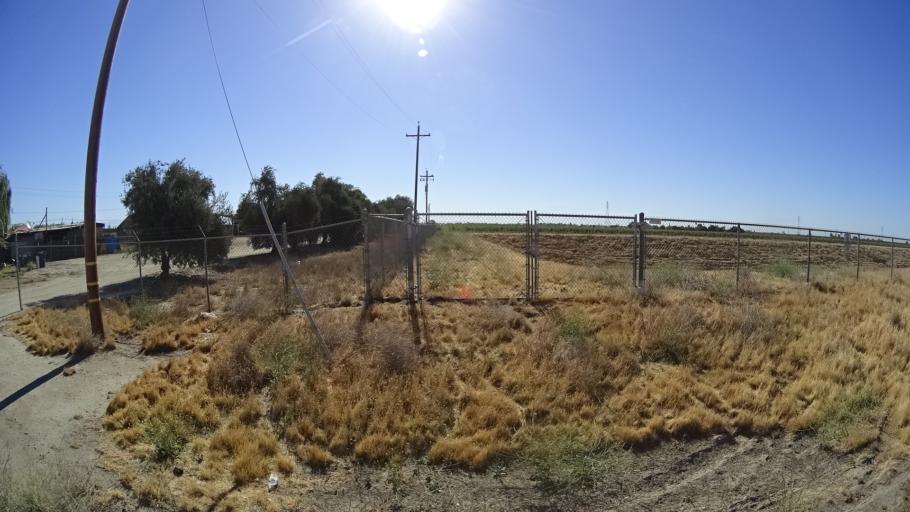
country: US
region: California
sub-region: Fresno County
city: West Park
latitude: 36.7057
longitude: -119.8267
